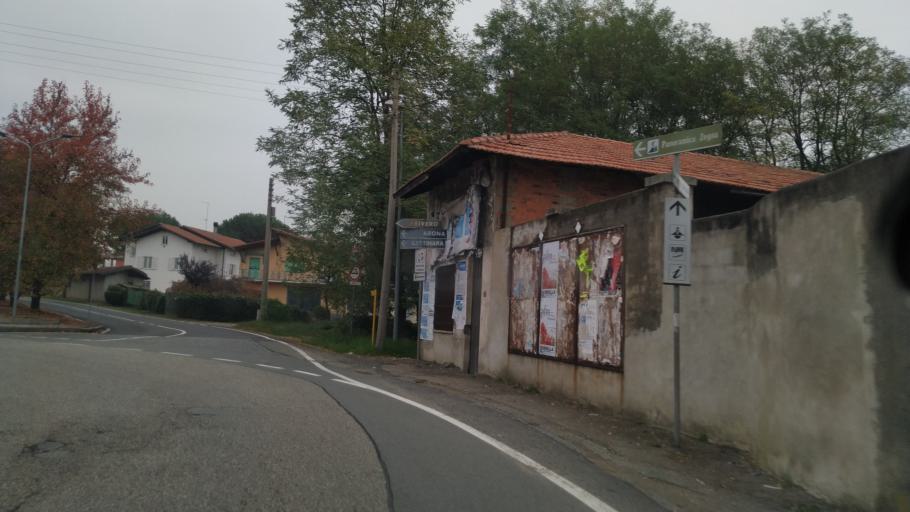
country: IT
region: Piedmont
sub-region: Provincia di Biella
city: Cossato
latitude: 45.5632
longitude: 8.1782
